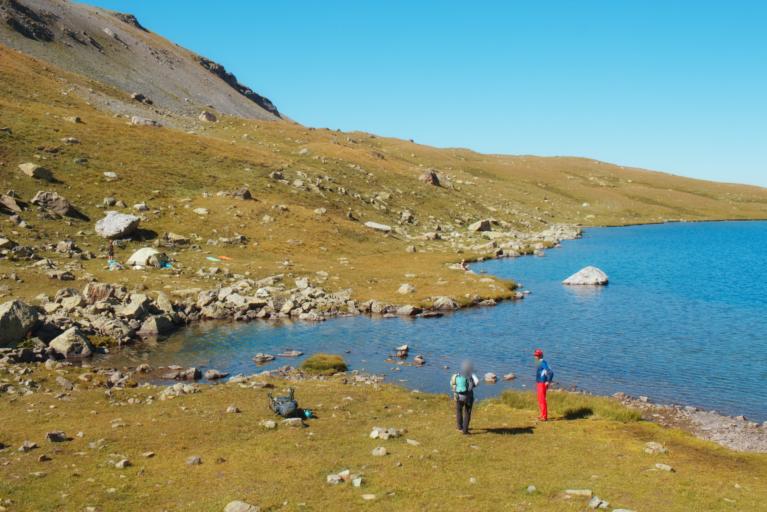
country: RU
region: Karachayevo-Cherkesiya
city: Nizhniy Arkhyz
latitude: 43.5958
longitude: 41.1939
